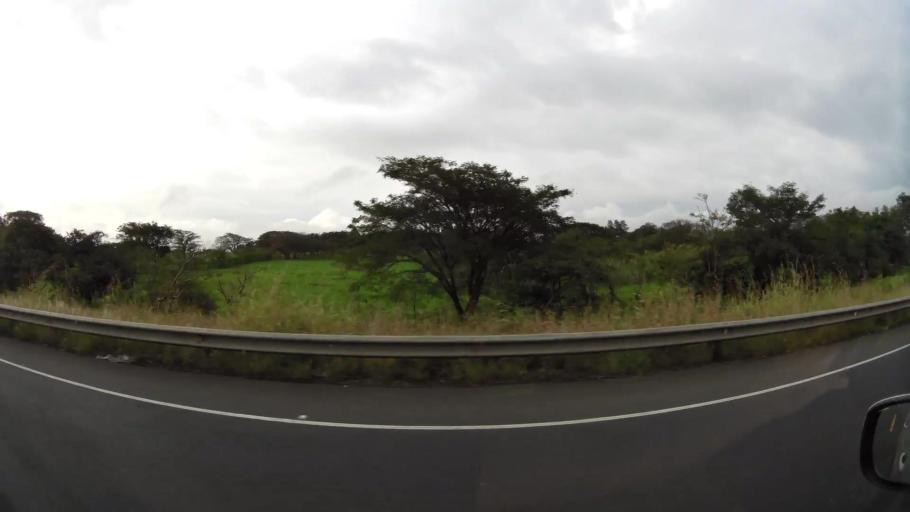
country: CR
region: Alajuela
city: Carrillos
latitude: 9.9648
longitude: -84.2949
